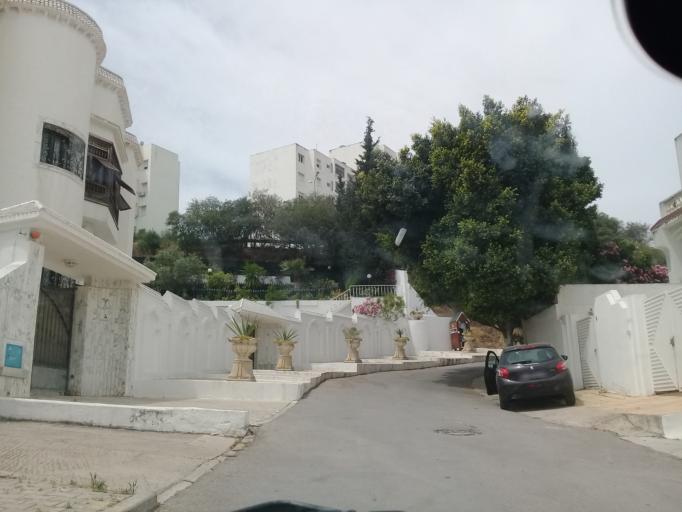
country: TN
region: Tunis
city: Tunis
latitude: 36.8378
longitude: 10.1524
